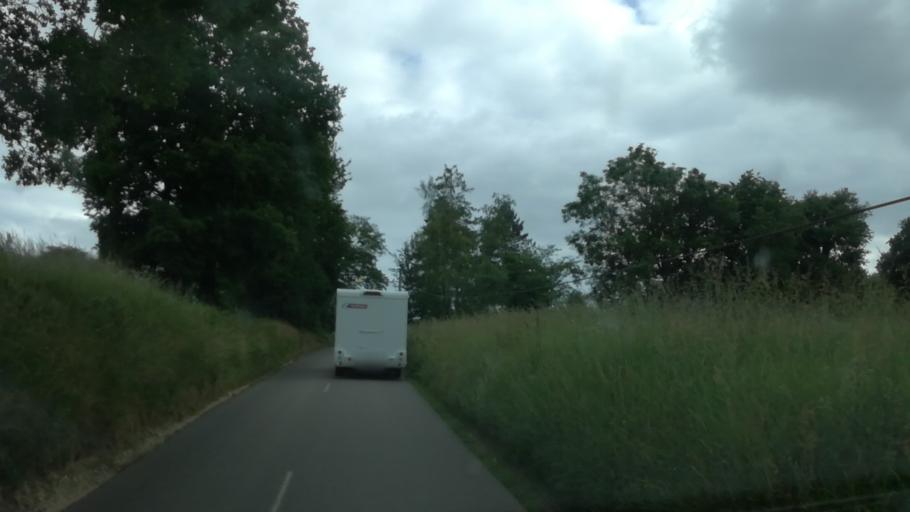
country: FR
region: Haute-Normandie
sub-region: Departement de l'Eure
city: Bourg-Achard
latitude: 49.3338
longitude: 0.8119
